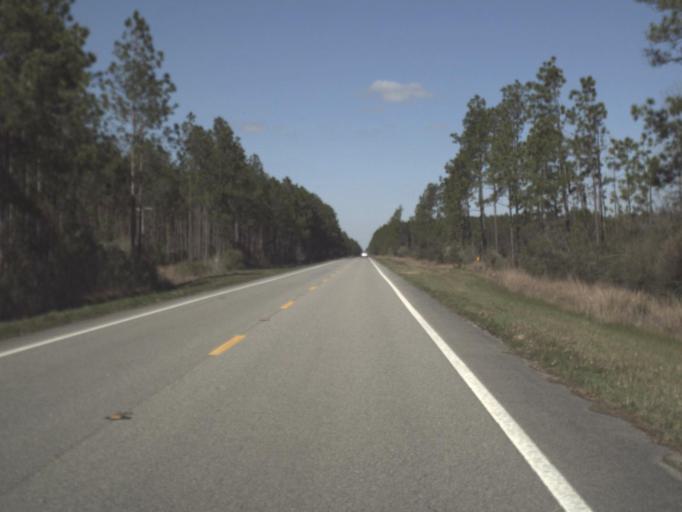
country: US
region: Florida
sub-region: Gulf County
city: Port Saint Joe
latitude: 29.9209
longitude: -85.1989
